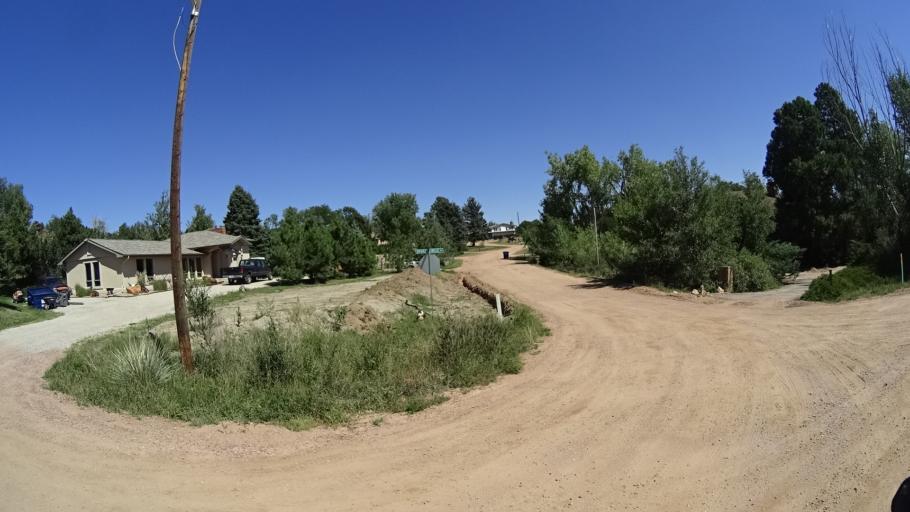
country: US
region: Colorado
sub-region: El Paso County
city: Cimarron Hills
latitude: 38.8640
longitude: -104.7376
